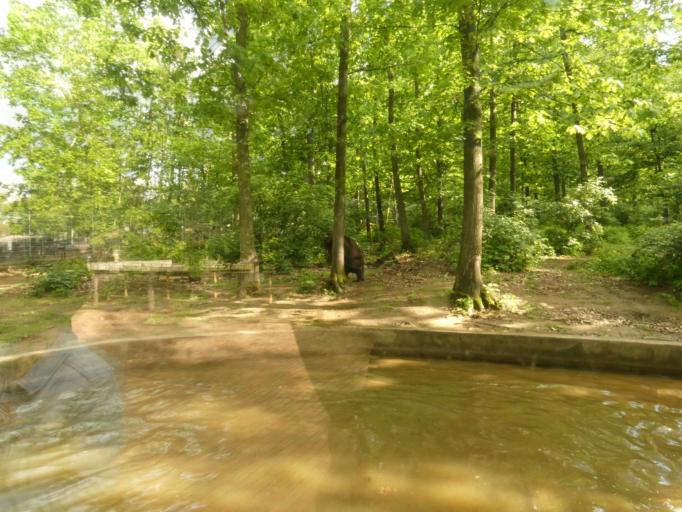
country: HU
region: Szabolcs-Szatmar-Bereg
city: Nyiregyhaza
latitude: 47.9970
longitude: 21.7252
